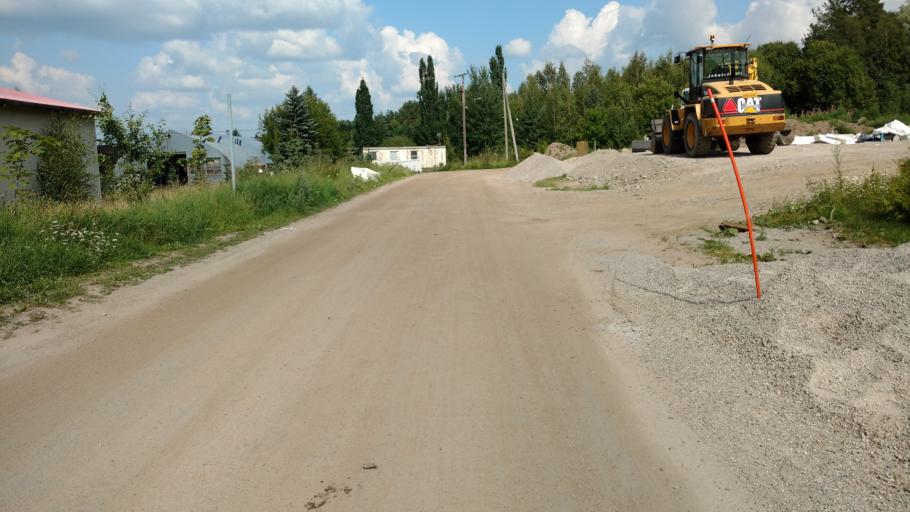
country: FI
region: Varsinais-Suomi
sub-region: Salo
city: Salo
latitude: 60.4091
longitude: 23.1902
